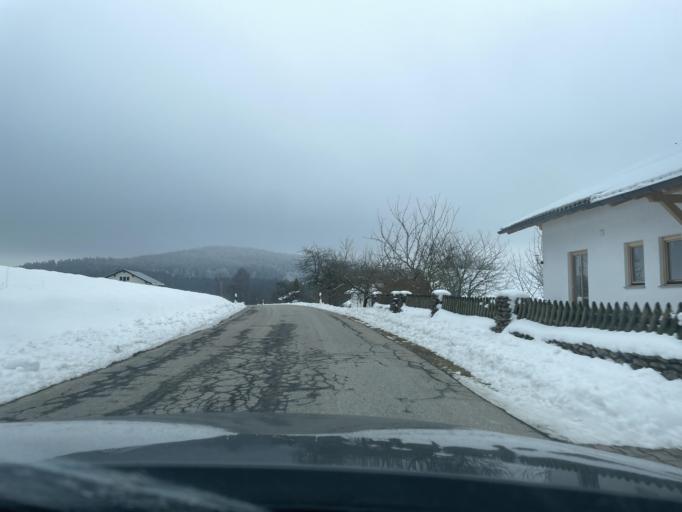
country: DE
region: Bavaria
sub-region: Lower Bavaria
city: Viechtach
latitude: 49.1234
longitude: 12.9295
